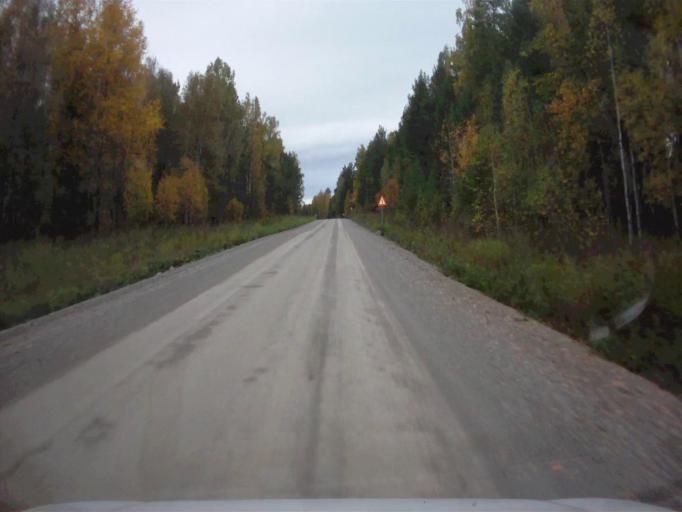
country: RU
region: Chelyabinsk
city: Nyazepetrovsk
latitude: 56.0836
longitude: 59.4206
